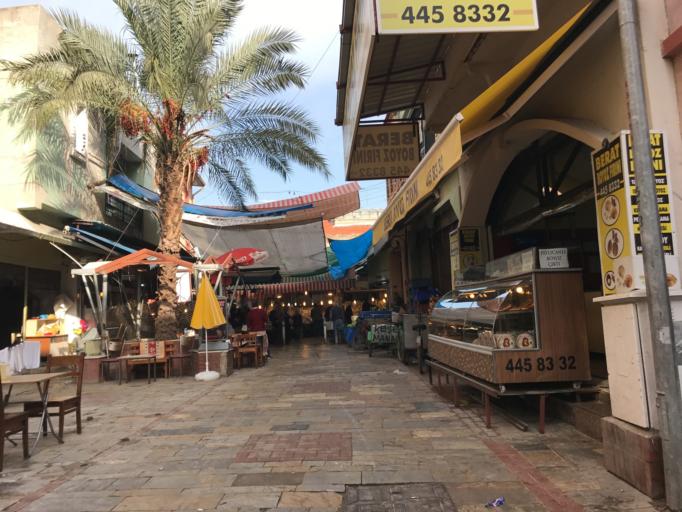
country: TR
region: Izmir
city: Izmir
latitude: 38.4194
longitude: 27.1361
